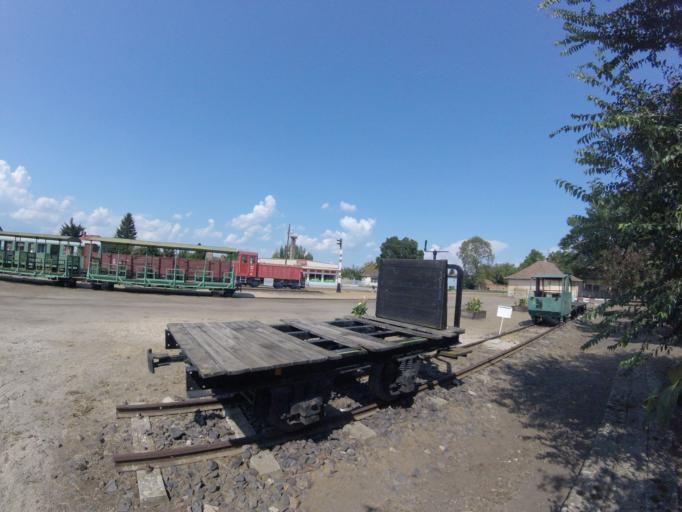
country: HU
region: Szabolcs-Szatmar-Bereg
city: Dombrad
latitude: 48.2250
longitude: 21.9220
